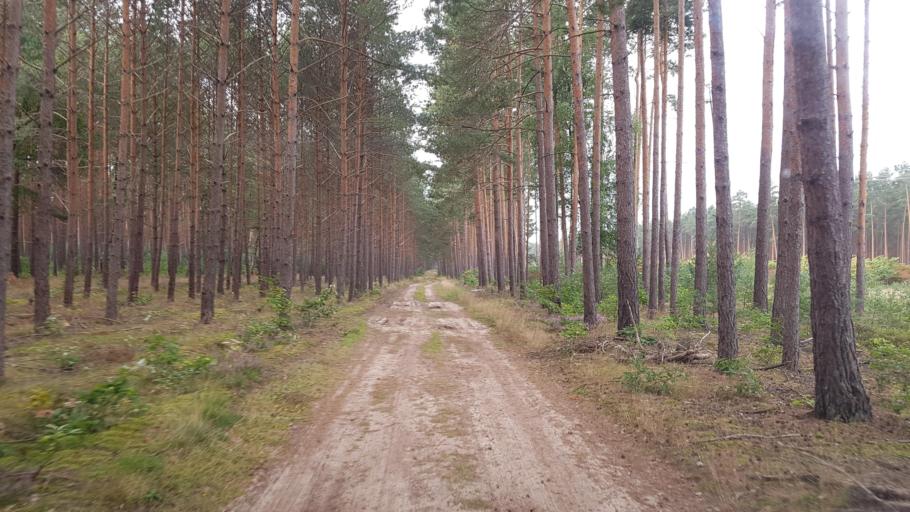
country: DE
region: Brandenburg
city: Hohenbucko
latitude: 51.7790
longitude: 13.5650
